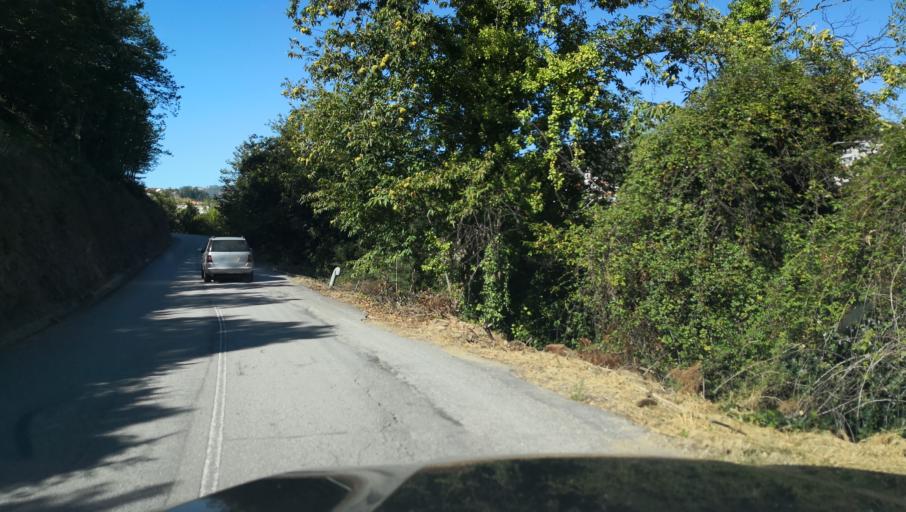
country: PT
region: Vila Real
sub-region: Santa Marta de Penaguiao
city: Santa Marta de Penaguiao
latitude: 41.2424
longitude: -7.8070
